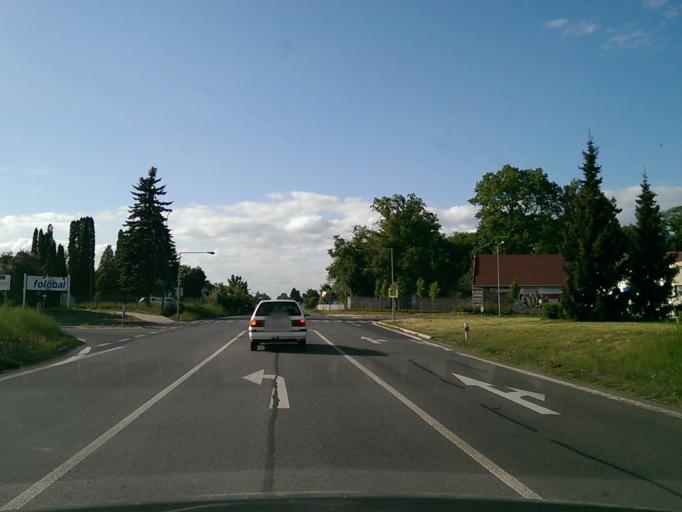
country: CZ
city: Doksy
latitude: 50.5624
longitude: 14.6510
